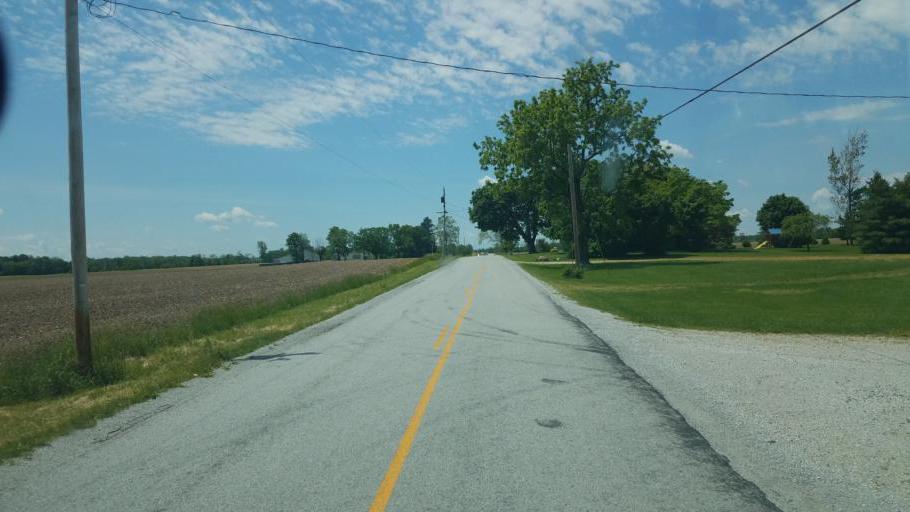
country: US
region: Ohio
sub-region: Hardin County
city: Forest
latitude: 40.6690
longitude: -83.4471
